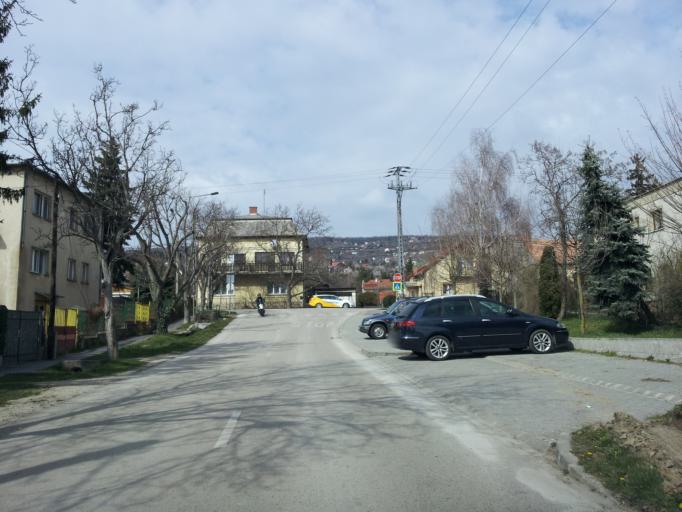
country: HU
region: Pest
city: Budaors
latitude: 47.4651
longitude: 18.9725
